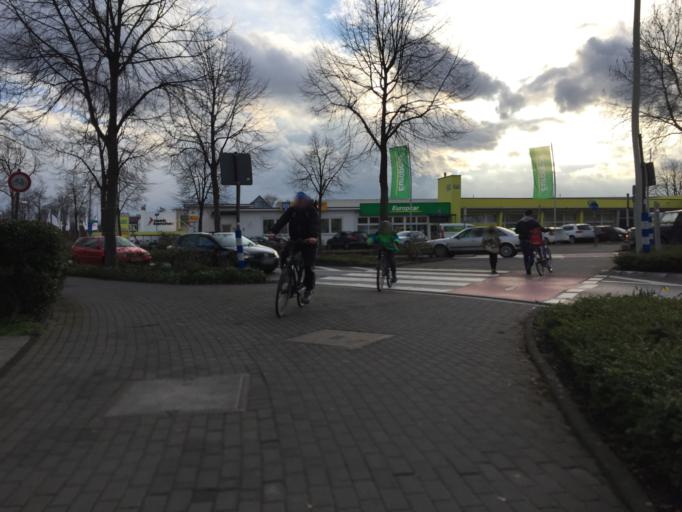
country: DE
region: North Rhine-Westphalia
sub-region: Regierungsbezirk Koln
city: Bonn
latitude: 50.7427
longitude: 7.0785
